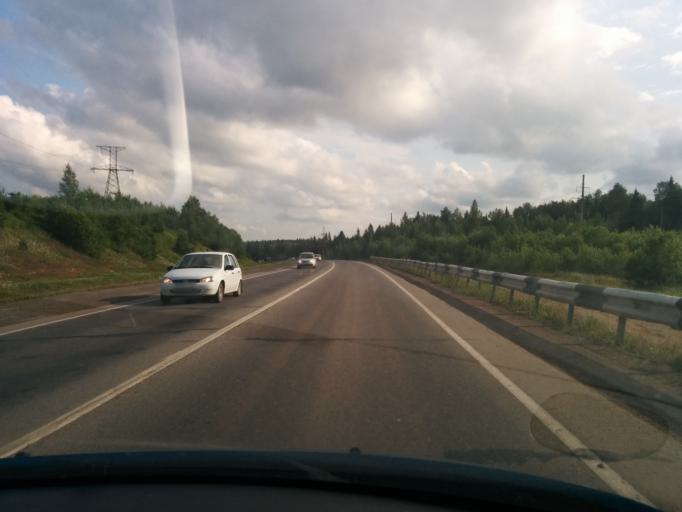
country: RU
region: Perm
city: Novyye Lyady
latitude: 58.0632
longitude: 56.4274
